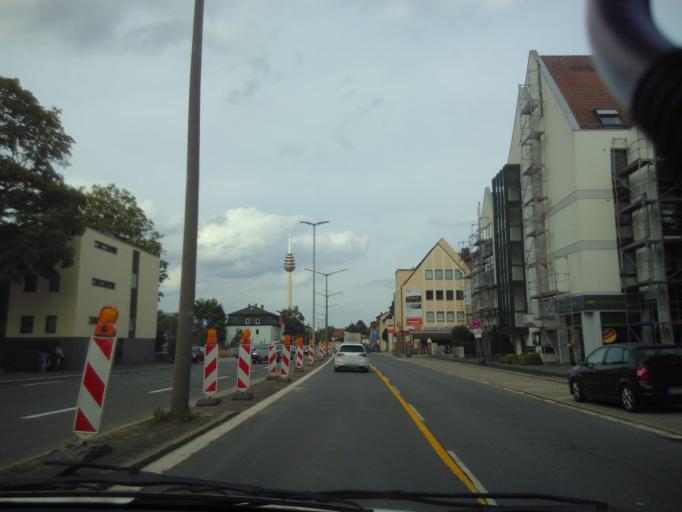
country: DE
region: Bavaria
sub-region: Regierungsbezirk Mittelfranken
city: Stein
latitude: 49.4184
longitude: 11.0221
